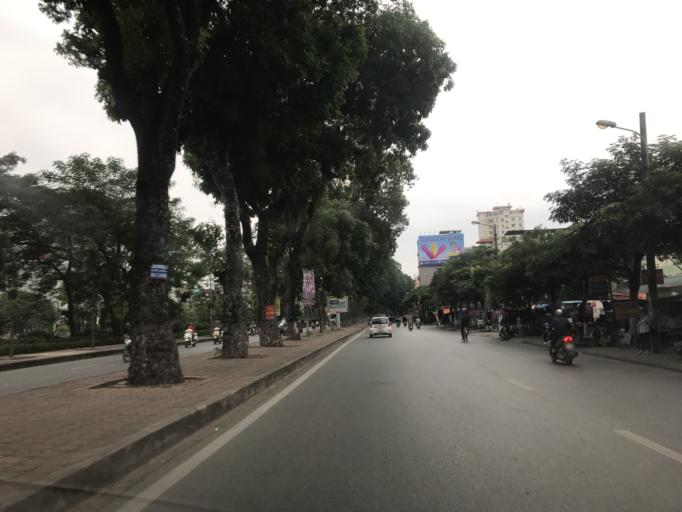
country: VN
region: Ha Noi
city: Thanh Xuan
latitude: 21.0130
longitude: 105.8080
